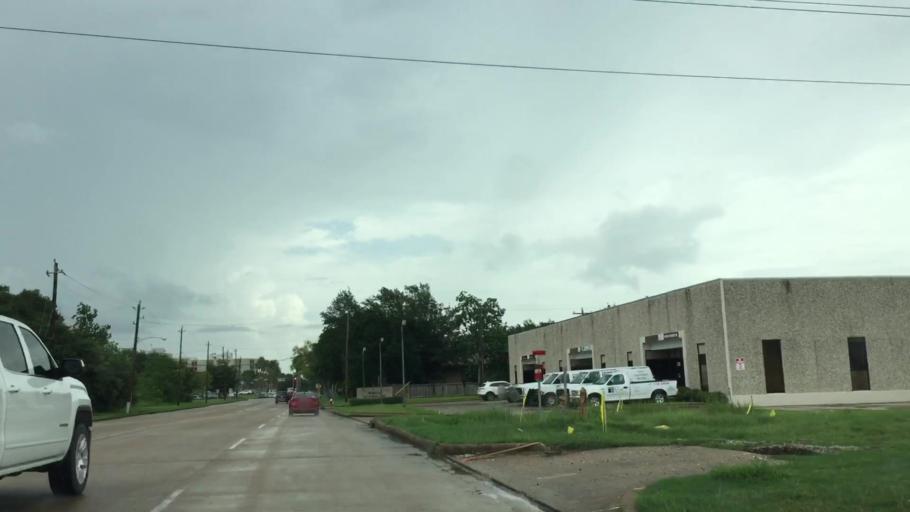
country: US
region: Texas
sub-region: Harris County
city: Webster
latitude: 29.5371
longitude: -95.1318
